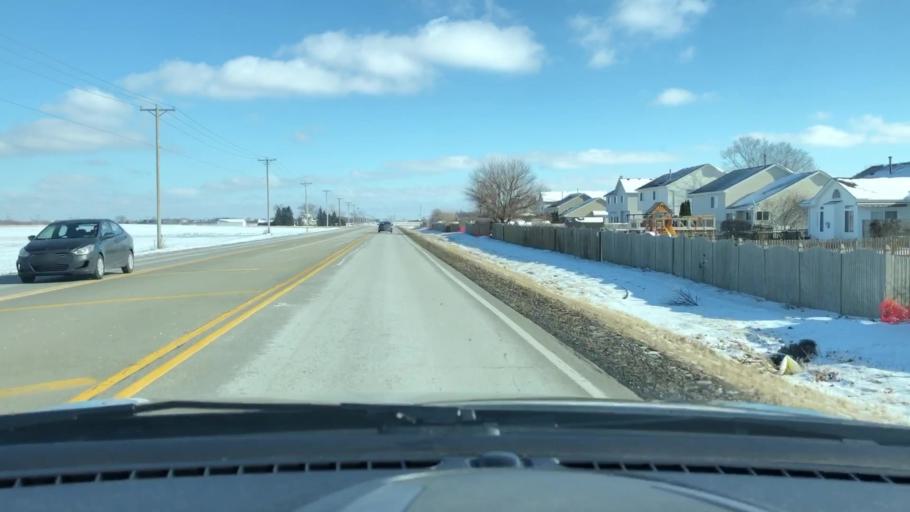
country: US
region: Illinois
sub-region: Will County
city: New Lenox
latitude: 41.4828
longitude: -87.9786
